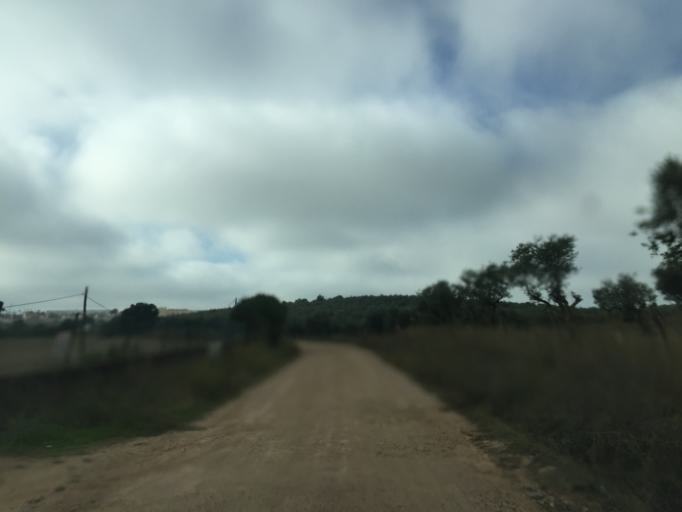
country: PT
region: Portalegre
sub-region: Fronteira
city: Fronteira
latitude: 39.0562
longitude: -7.6360
